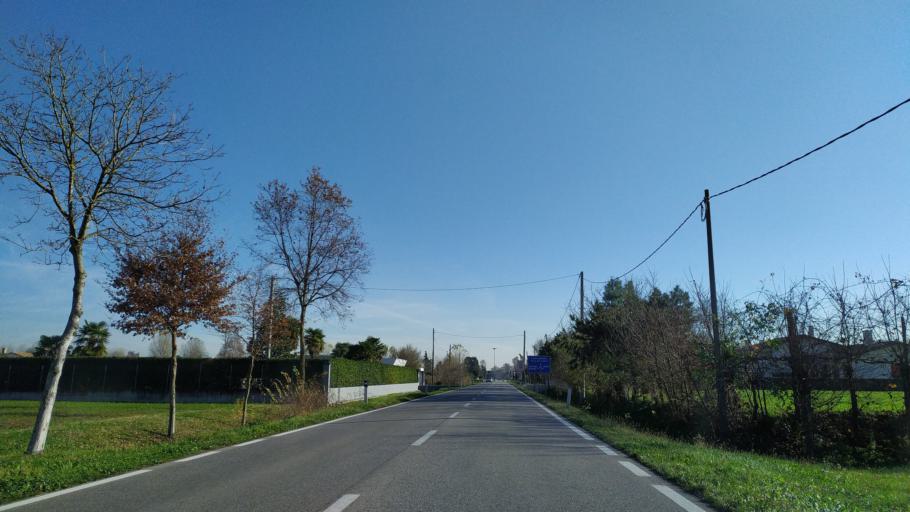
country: IT
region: Veneto
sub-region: Provincia di Padova
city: Villa del Conte
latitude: 45.5867
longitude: 11.8409
